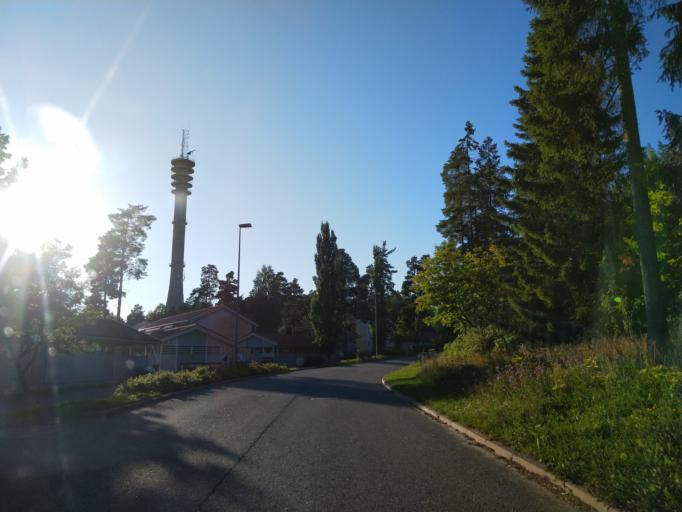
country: FI
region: Varsinais-Suomi
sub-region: Turku
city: Kaarina
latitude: 60.4459
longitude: 22.3373
